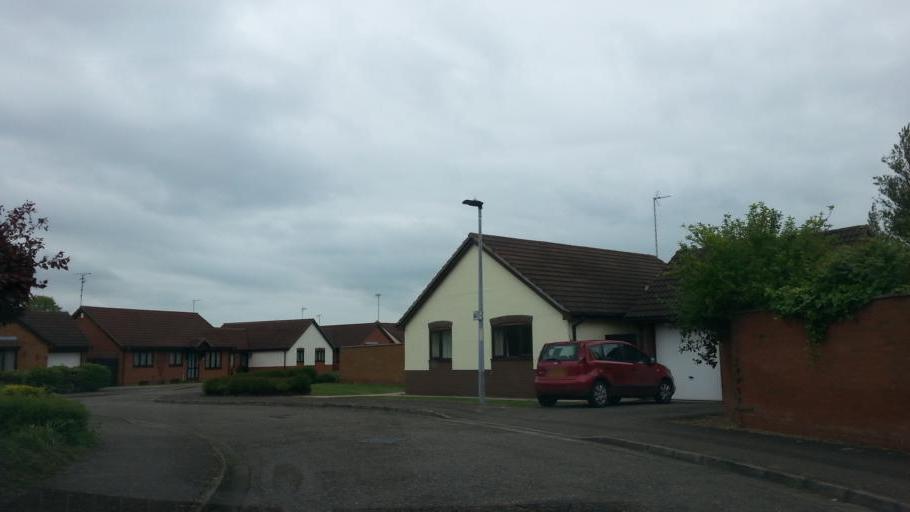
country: GB
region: England
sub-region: Peterborough
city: Peterborough
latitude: 52.5699
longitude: -0.2511
